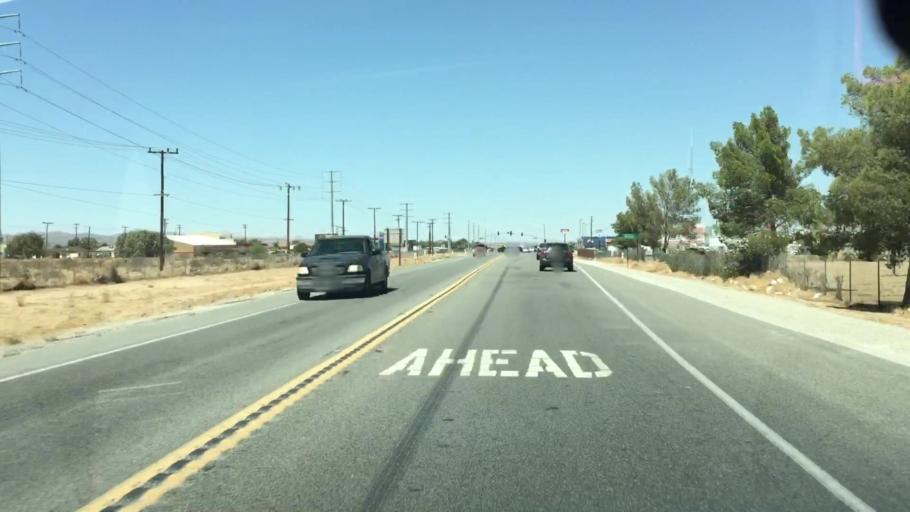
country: US
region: California
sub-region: San Bernardino County
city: Adelanto
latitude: 34.5764
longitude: -117.4111
